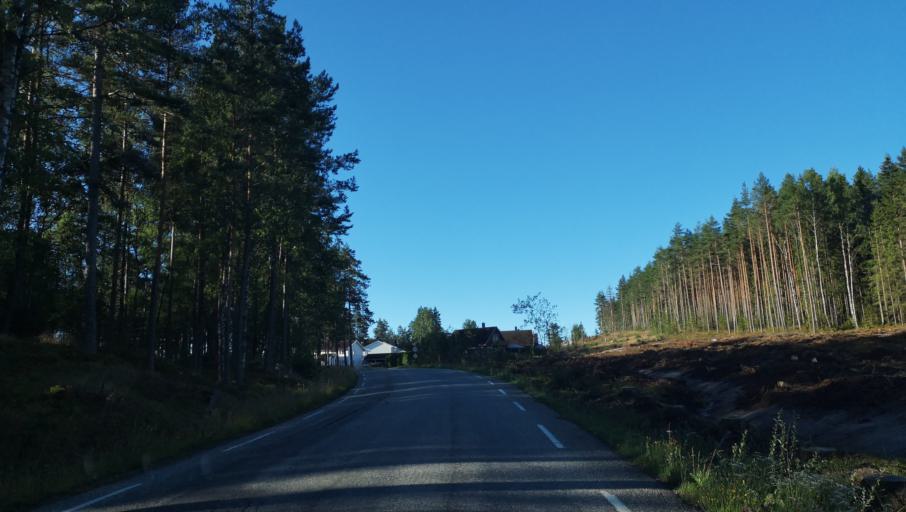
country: NO
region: Ostfold
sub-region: Hobol
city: Knappstad
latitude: 59.6331
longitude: 11.0241
